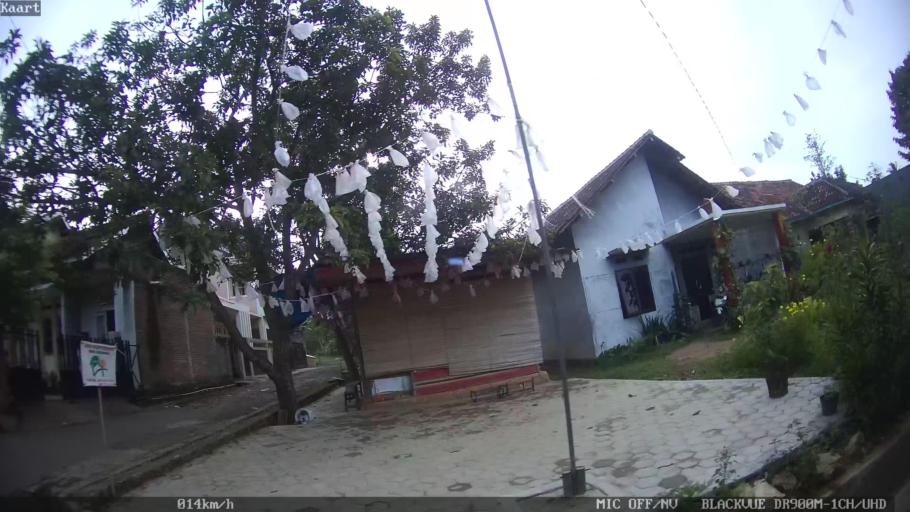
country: ID
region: Lampung
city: Kedaton
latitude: -5.3937
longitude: 105.2036
